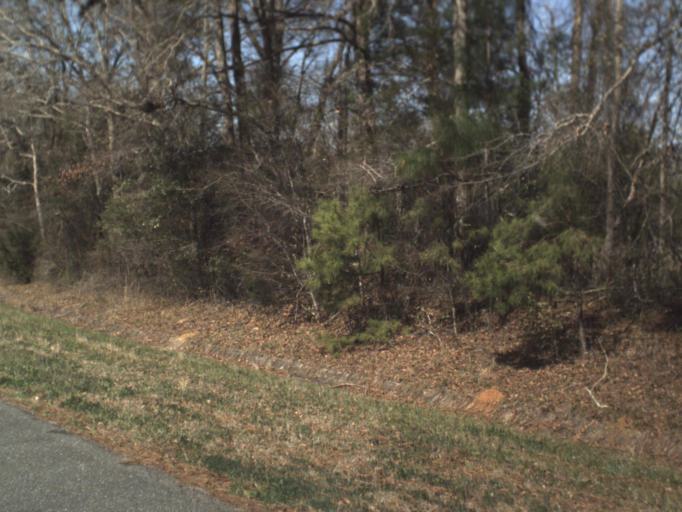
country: US
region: Florida
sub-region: Jackson County
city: Marianna
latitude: 30.7851
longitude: -85.3412
